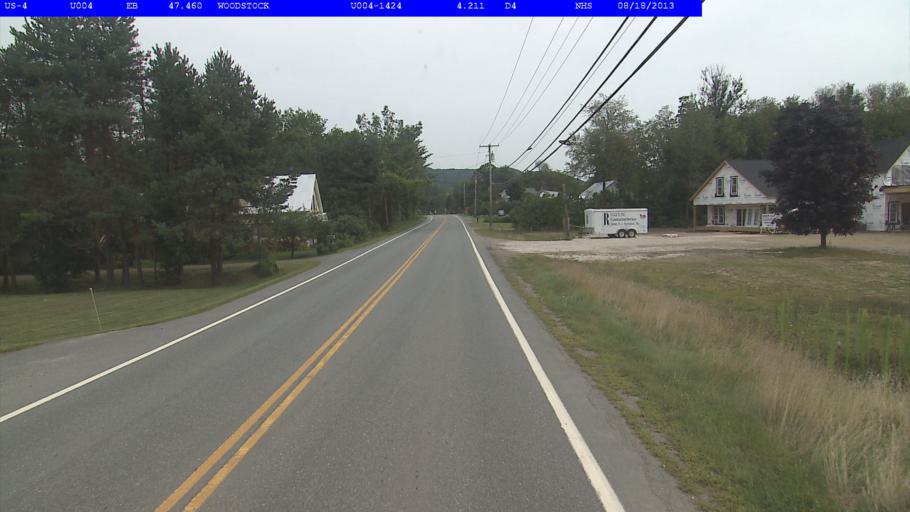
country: US
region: Vermont
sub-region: Windsor County
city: Woodstock
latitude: 43.6094
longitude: -72.5507
